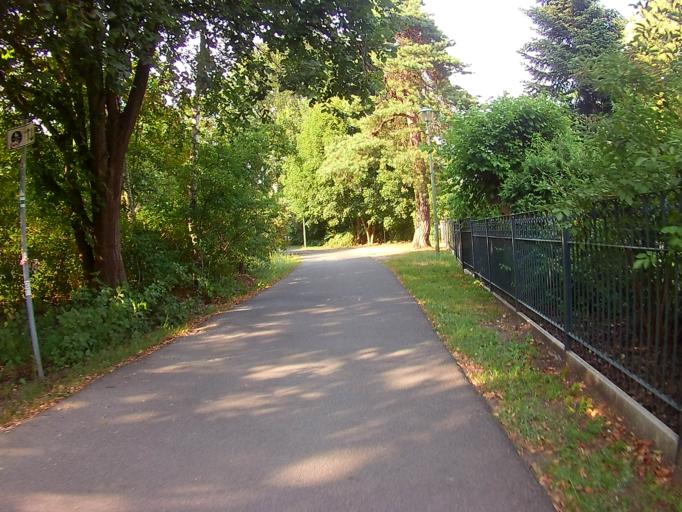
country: DE
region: Berlin
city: Kopenick Bezirk
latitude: 52.4722
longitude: 13.5676
